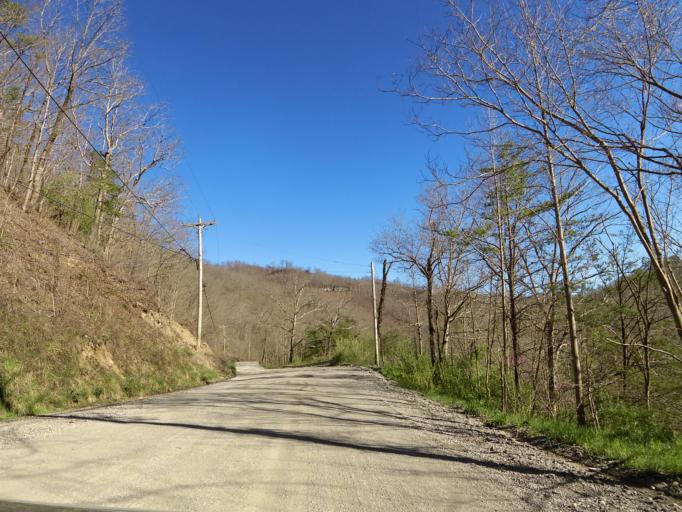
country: US
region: Tennessee
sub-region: Scott County
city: Huntsville
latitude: 36.3125
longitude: -84.3843
